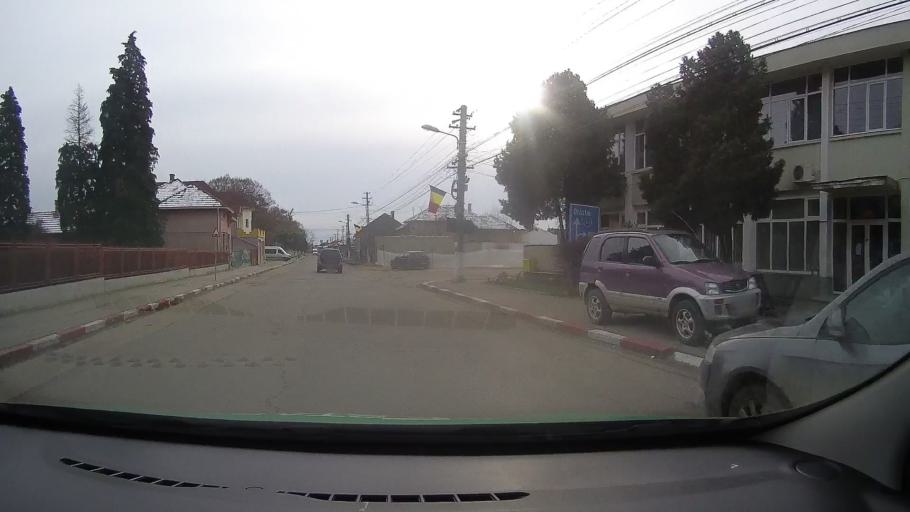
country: RO
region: Hunedoara
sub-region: Comuna Geoagiu
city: Geoagiu
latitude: 45.9195
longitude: 23.1997
